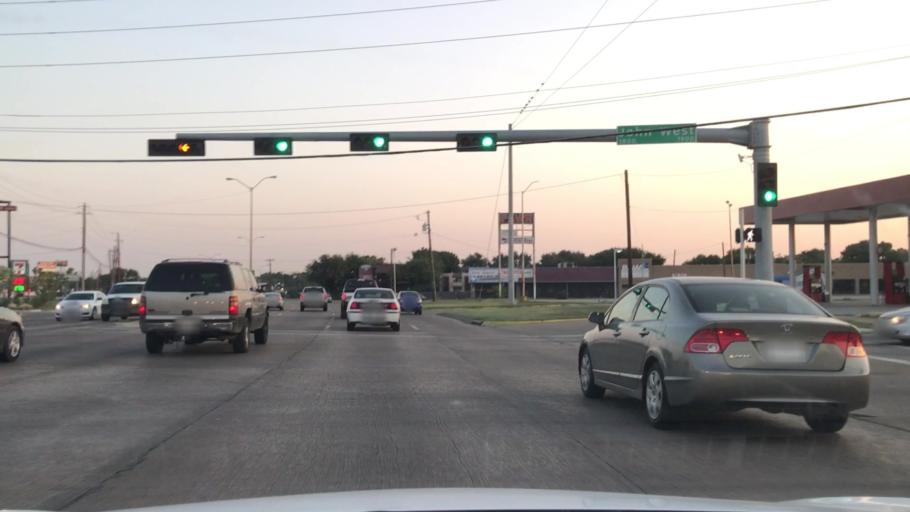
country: US
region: Texas
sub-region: Dallas County
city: Mesquite
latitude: 32.8070
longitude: -96.6826
